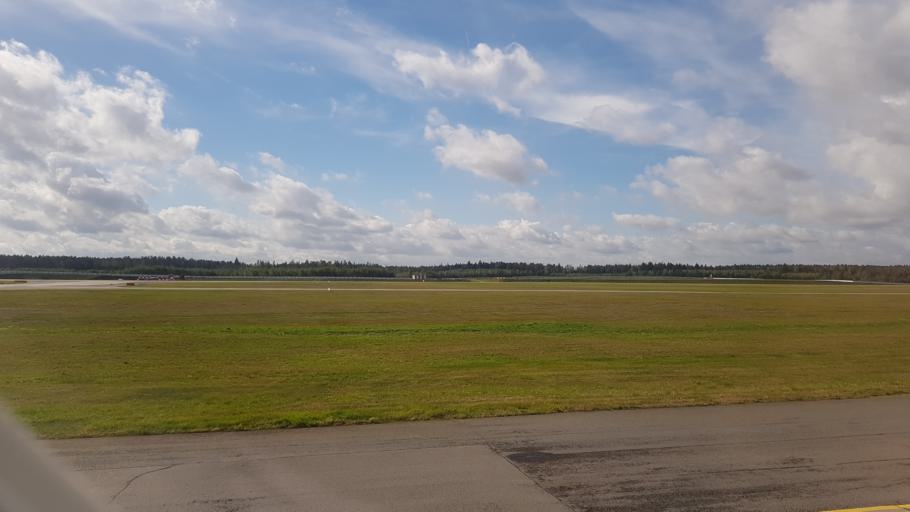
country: BY
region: Minsk
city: Smilavichy
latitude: 53.8855
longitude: 28.0342
